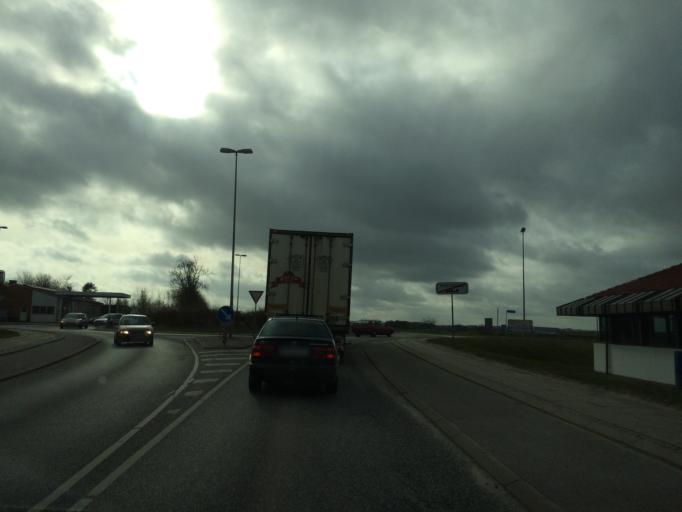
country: DK
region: Central Jutland
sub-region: Favrskov Kommune
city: Ulstrup
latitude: 56.4998
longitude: 9.7432
